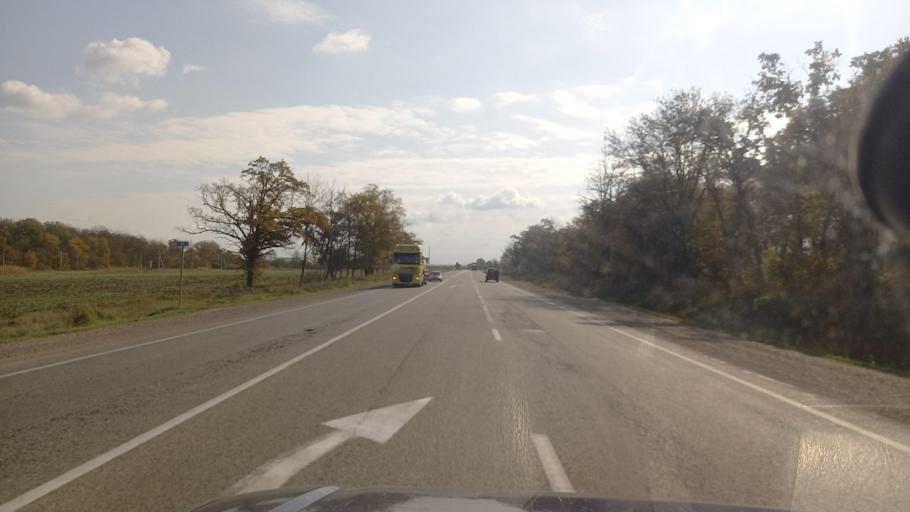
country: RU
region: Krasnodarskiy
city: Abinsk
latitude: 44.8771
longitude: 38.1066
